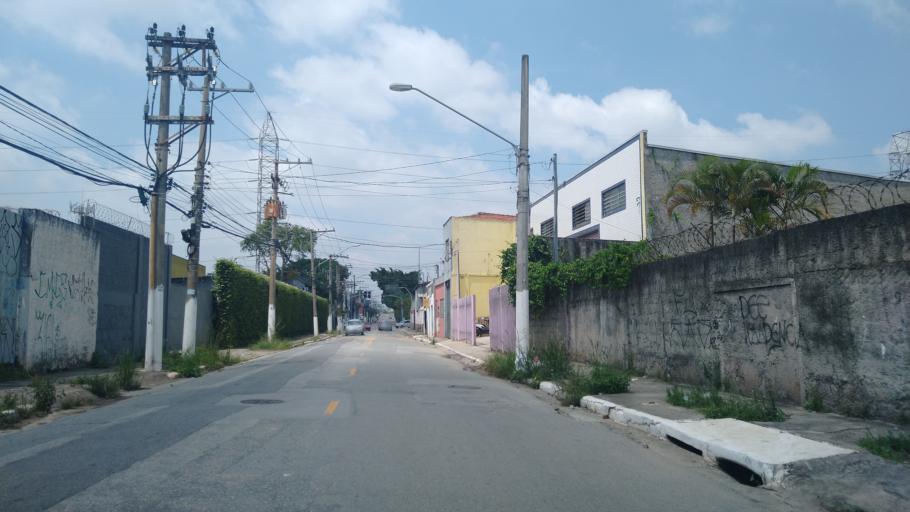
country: BR
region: Sao Paulo
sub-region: Sao Paulo
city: Sao Paulo
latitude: -23.5071
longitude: -46.6119
